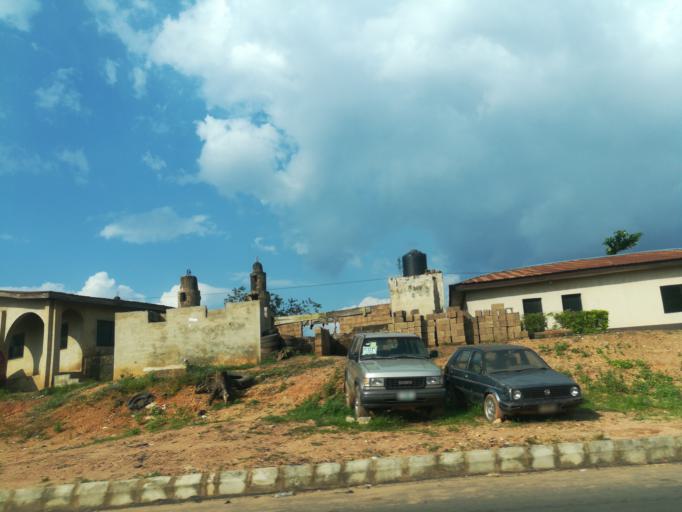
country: NG
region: Oyo
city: Ibadan
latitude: 7.4195
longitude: 3.8483
